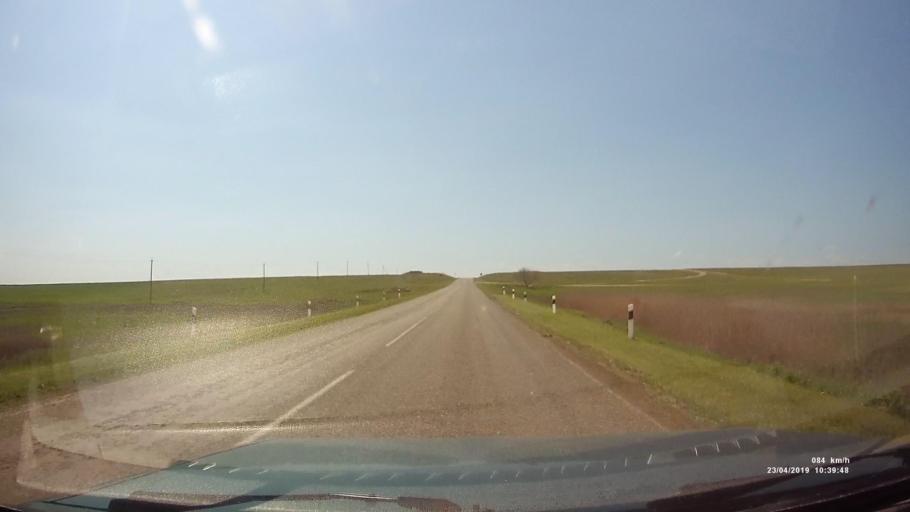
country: RU
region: Kalmykiya
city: Yashalta
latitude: 46.5146
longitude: 42.6386
